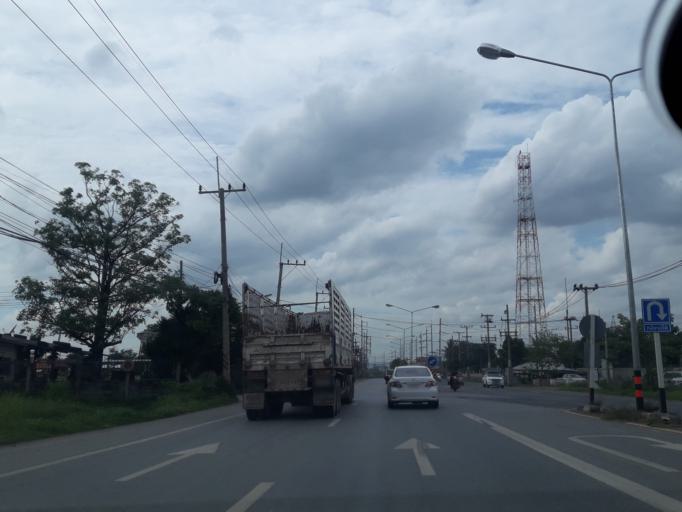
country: TH
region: Sara Buri
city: Kaeng Khoi
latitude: 14.5648
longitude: 101.0070
